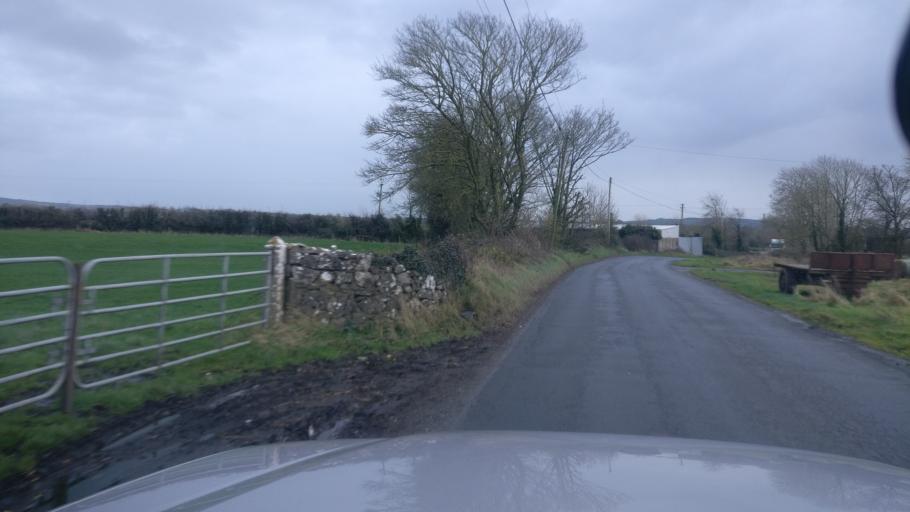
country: IE
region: Munster
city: Nenagh Bridge
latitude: 52.9880
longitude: -8.1147
